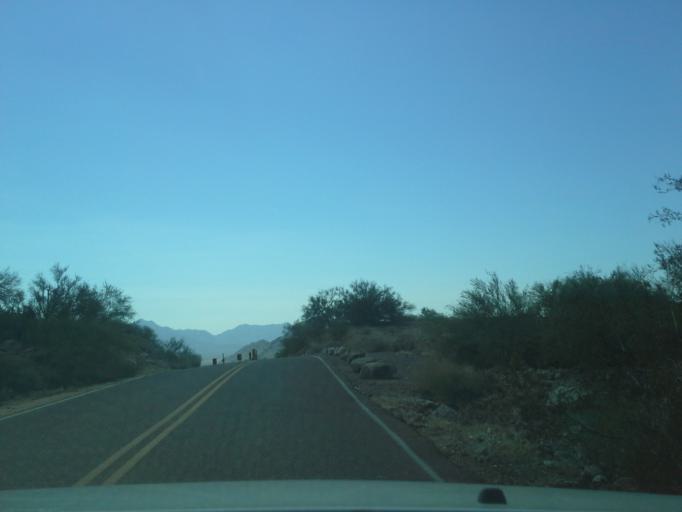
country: US
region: Arizona
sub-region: Maricopa County
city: Laveen
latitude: 33.3361
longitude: -112.0688
